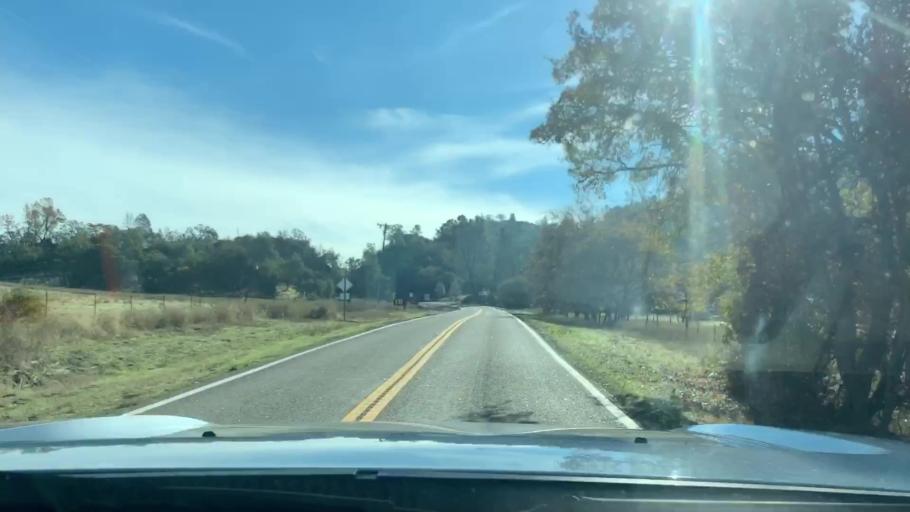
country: US
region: California
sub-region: Fresno County
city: Coalinga
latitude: 36.1691
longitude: -120.6674
